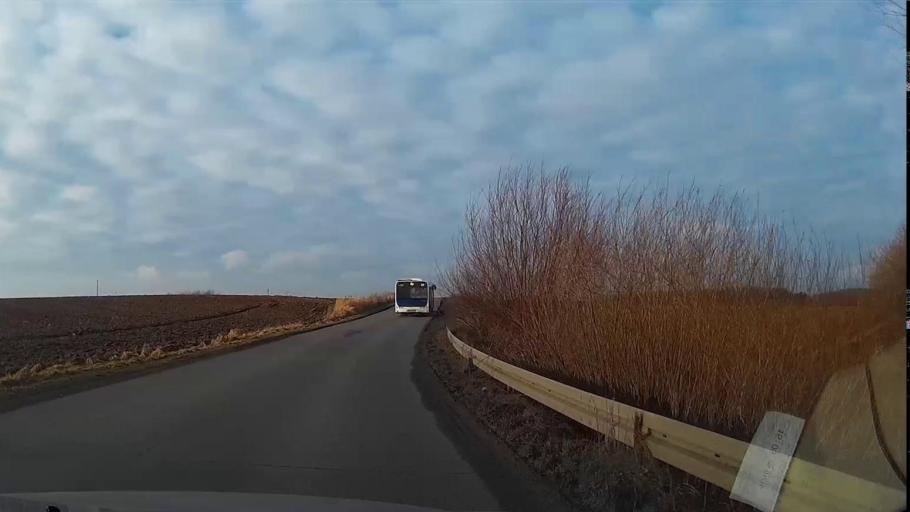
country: PL
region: Lesser Poland Voivodeship
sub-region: Powiat krakowski
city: Sanka
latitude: 50.0623
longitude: 19.6656
